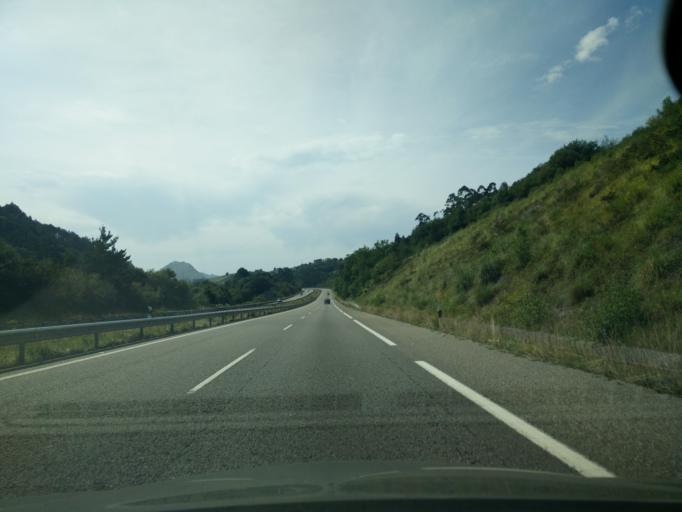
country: ES
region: Asturias
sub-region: Province of Asturias
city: Ribadesella
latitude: 43.4370
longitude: -5.0707
